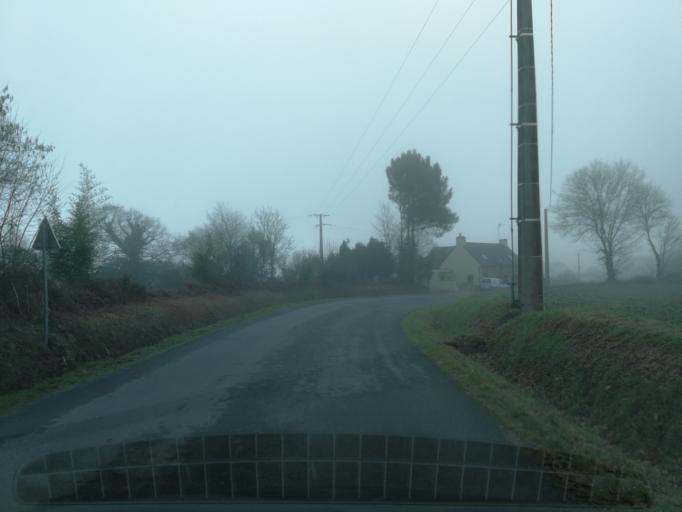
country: FR
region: Brittany
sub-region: Departement du Morbihan
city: La Vraie-Croix
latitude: 47.7373
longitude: -2.5022
